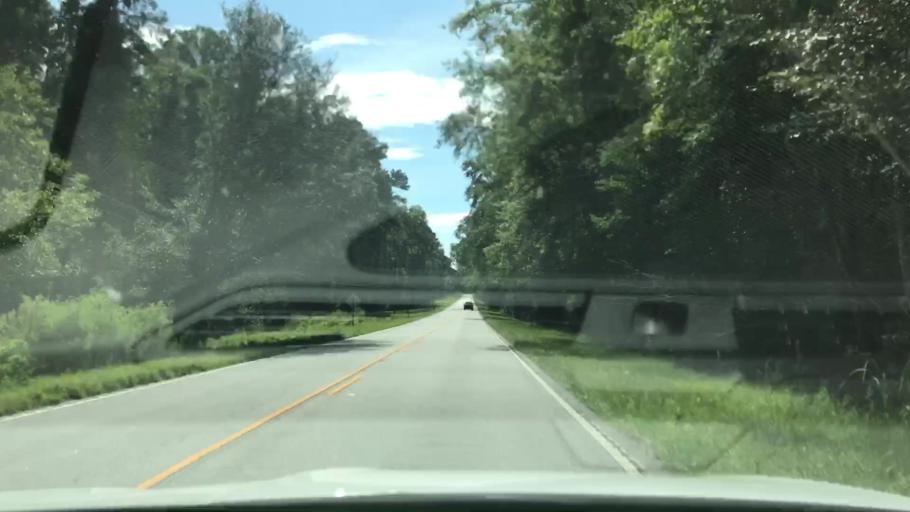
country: US
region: South Carolina
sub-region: Dorchester County
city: Centerville
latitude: 32.9445
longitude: -80.1945
